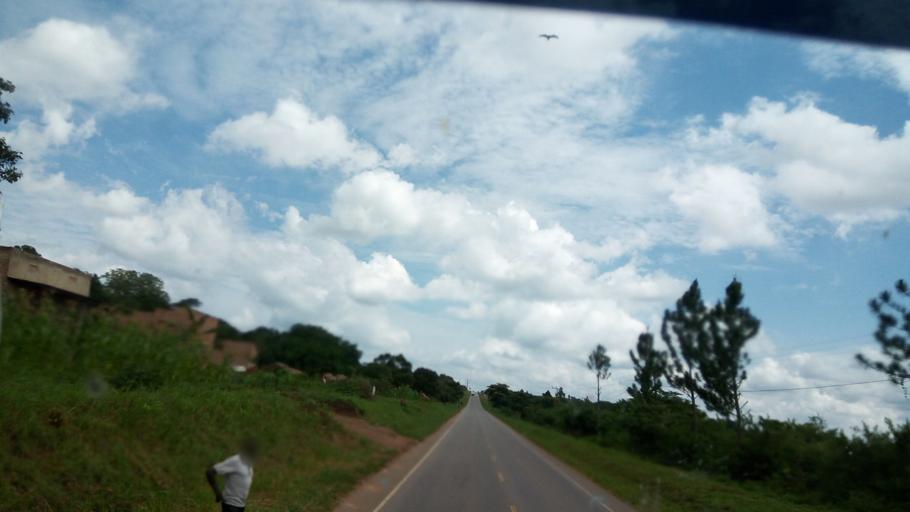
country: UG
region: Central Region
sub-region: Nakasongola District
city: Nakasongola
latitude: 1.2722
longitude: 32.4422
